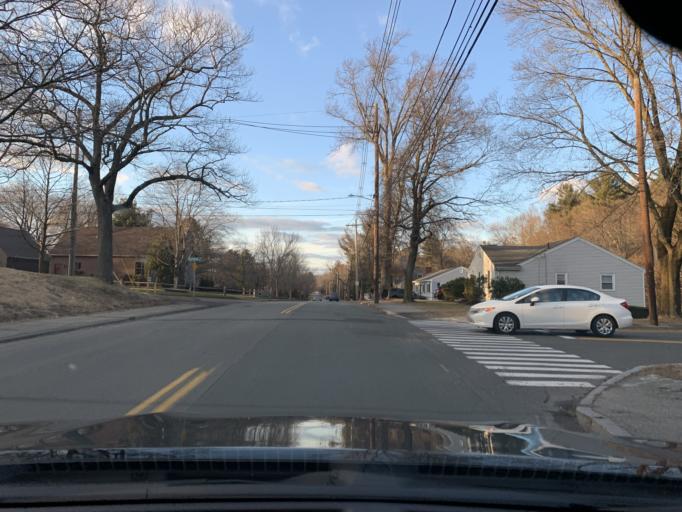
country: US
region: Massachusetts
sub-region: Essex County
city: Lynnfield
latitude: 42.5163
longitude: -71.0136
